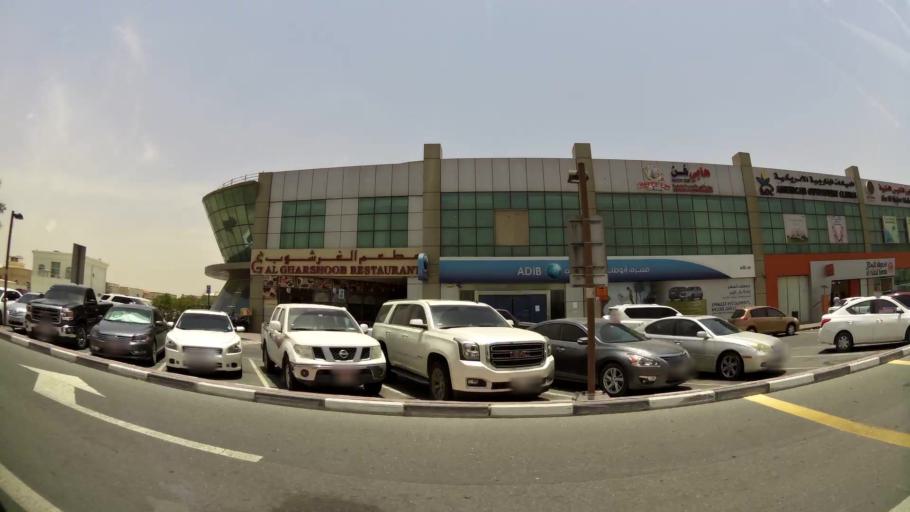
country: AE
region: Ash Shariqah
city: Sharjah
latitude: 25.2135
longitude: 55.3810
